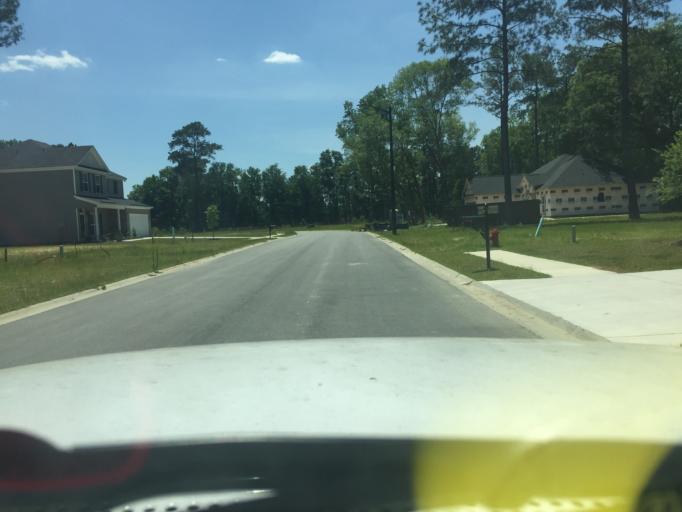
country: US
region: Georgia
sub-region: Chatham County
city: Georgetown
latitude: 32.0273
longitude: -81.2114
